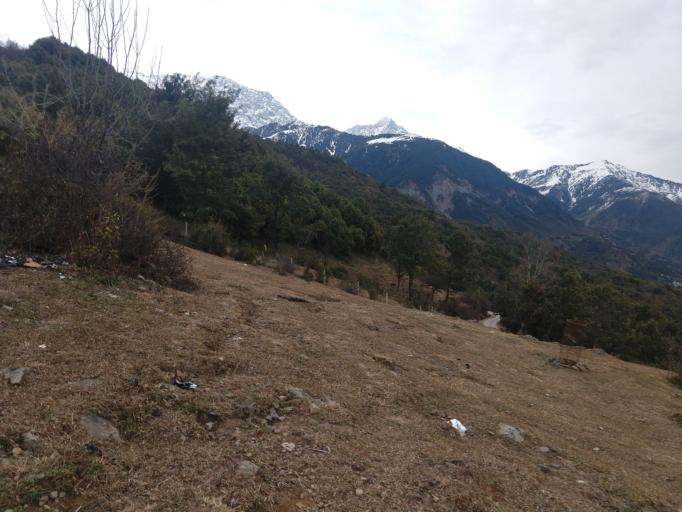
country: IN
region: Himachal Pradesh
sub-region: Kangra
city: Dharmsala
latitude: 32.2215
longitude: 76.3367
